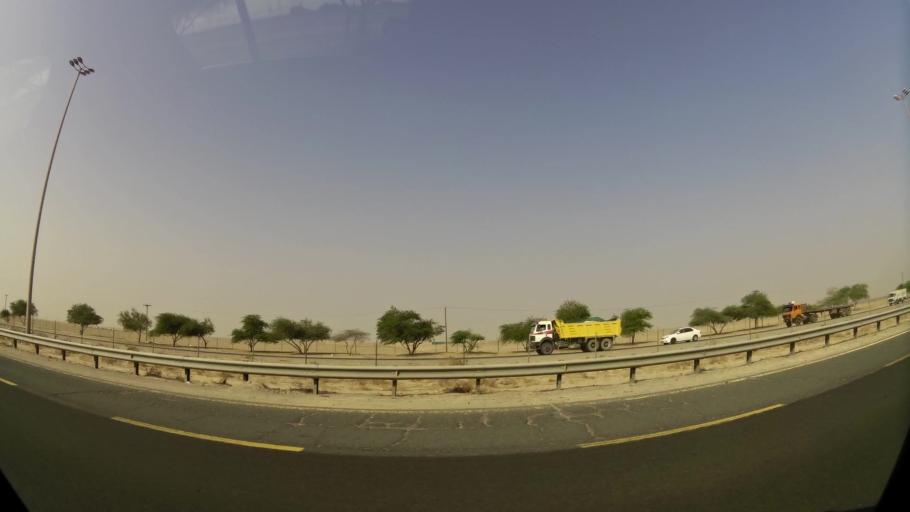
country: KW
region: Al Asimah
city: Ar Rabiyah
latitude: 29.2159
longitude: 47.8849
